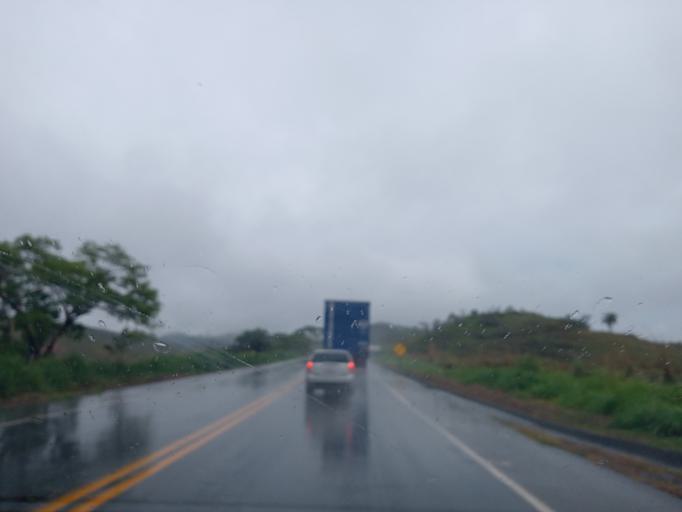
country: BR
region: Minas Gerais
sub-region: Luz
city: Luz
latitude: -19.7247
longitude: -45.8701
